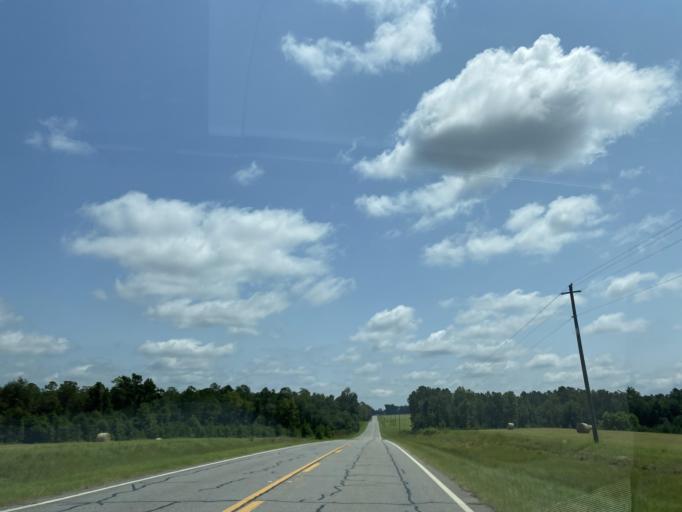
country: US
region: Georgia
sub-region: Wilcox County
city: Abbeville
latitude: 32.0046
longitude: -83.1340
